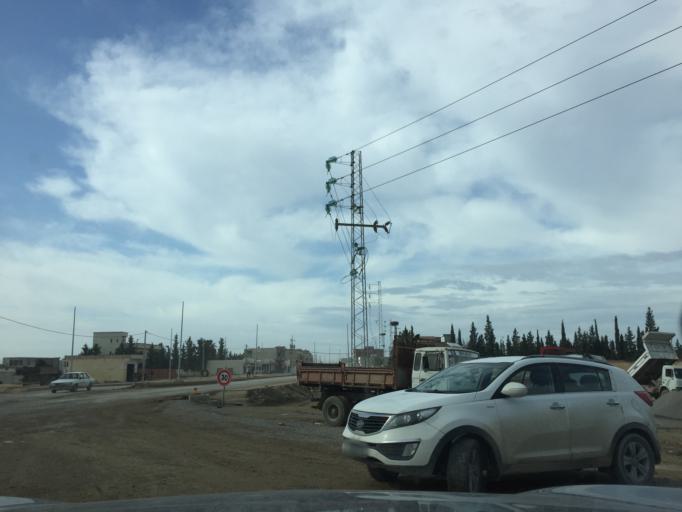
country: TN
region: Zaghwan
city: El Fahs
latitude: 36.3702
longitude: 9.8991
